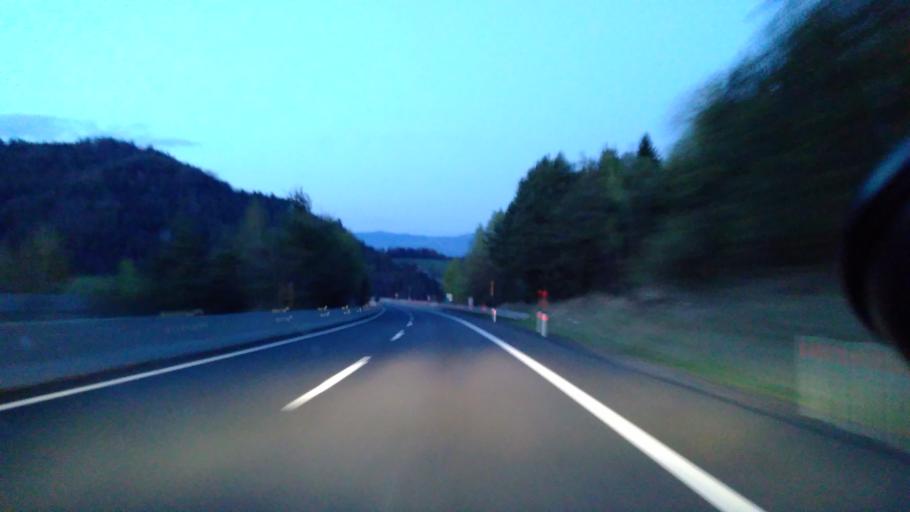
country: AT
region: Carinthia
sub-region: Politischer Bezirk Wolfsberg
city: Sankt Andrae
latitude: 46.7209
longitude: 14.7961
